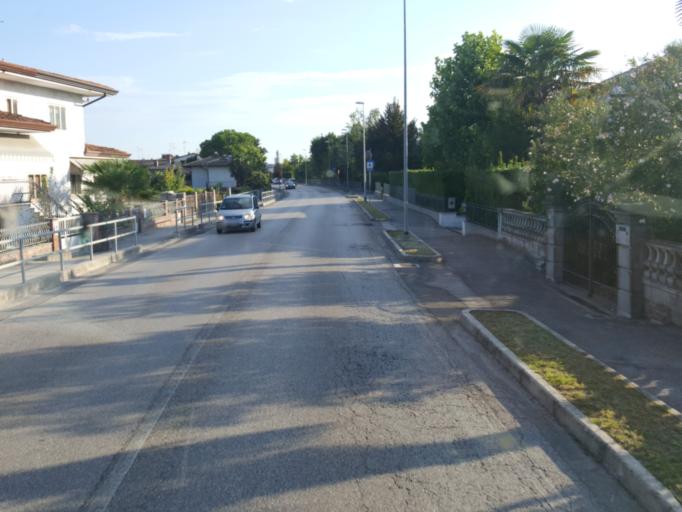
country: IT
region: Friuli Venezia Giulia
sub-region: Provincia di Udine
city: Porpetto
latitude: 45.8539
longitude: 13.2144
